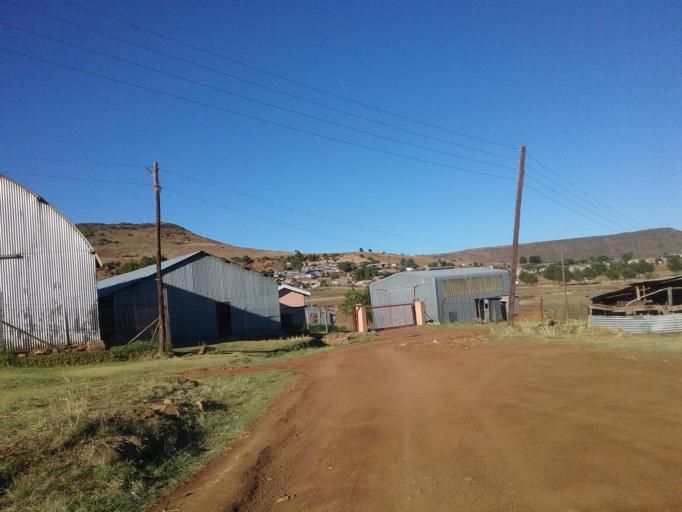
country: LS
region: Quthing
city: Quthing
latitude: -30.4087
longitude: 27.6996
